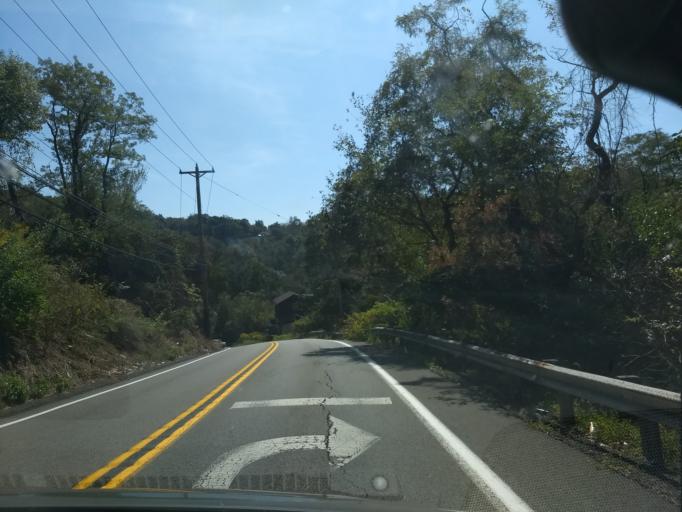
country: US
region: Pennsylvania
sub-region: Allegheny County
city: North Versailles
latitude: 40.3640
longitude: -79.8266
